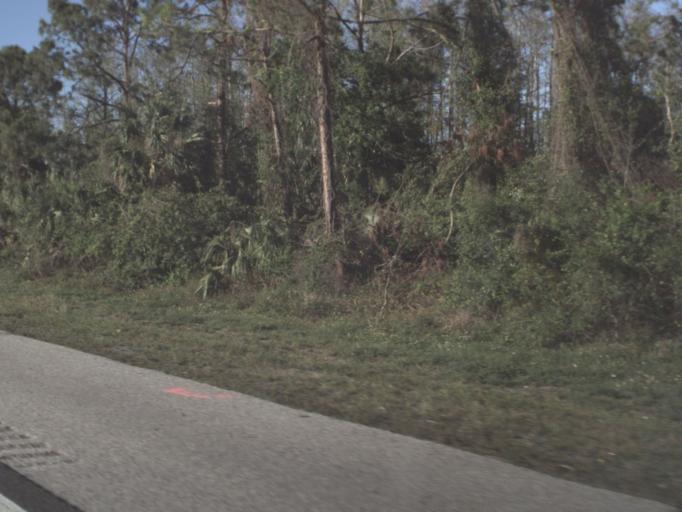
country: US
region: Florida
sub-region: Flagler County
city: Flagler Beach
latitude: 29.4061
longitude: -81.1560
